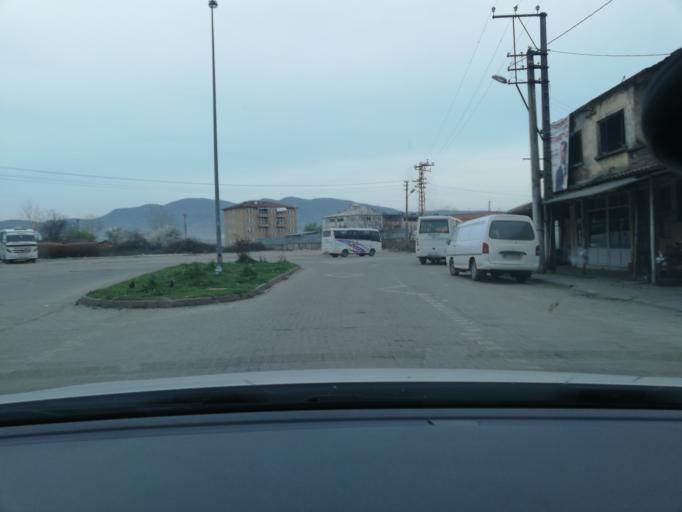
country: TR
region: Zonguldak
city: Caycuma
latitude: 41.4168
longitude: 32.0941
